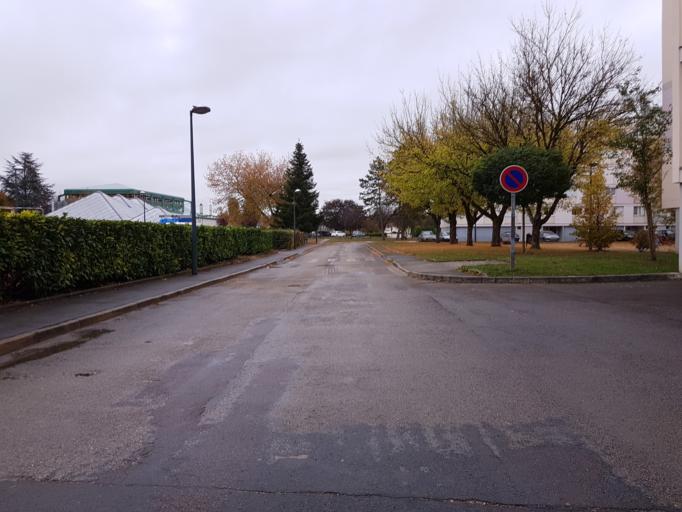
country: FR
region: Bourgogne
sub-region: Departement de la Cote-d'Or
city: Chevigny-Saint-Sauveur
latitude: 47.2991
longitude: 5.1379
